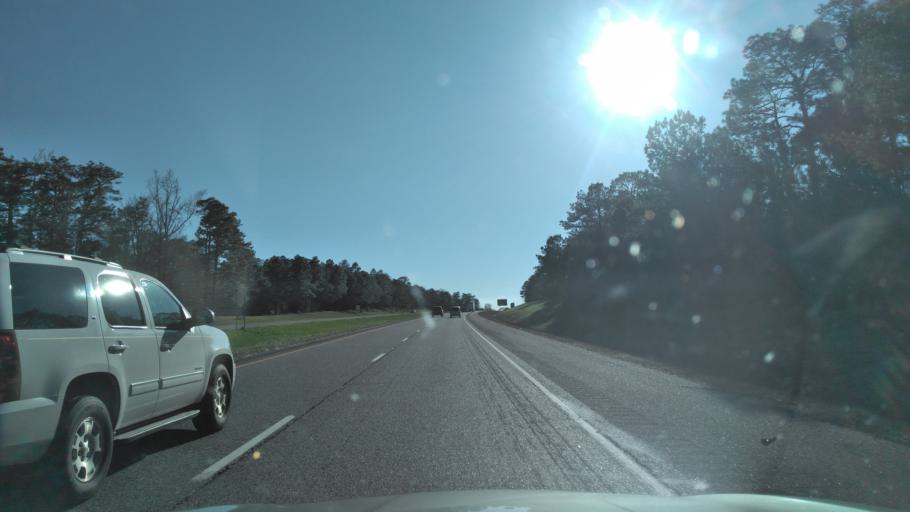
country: US
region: Alabama
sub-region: Escambia County
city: Atmore
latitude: 31.1179
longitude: -87.4566
